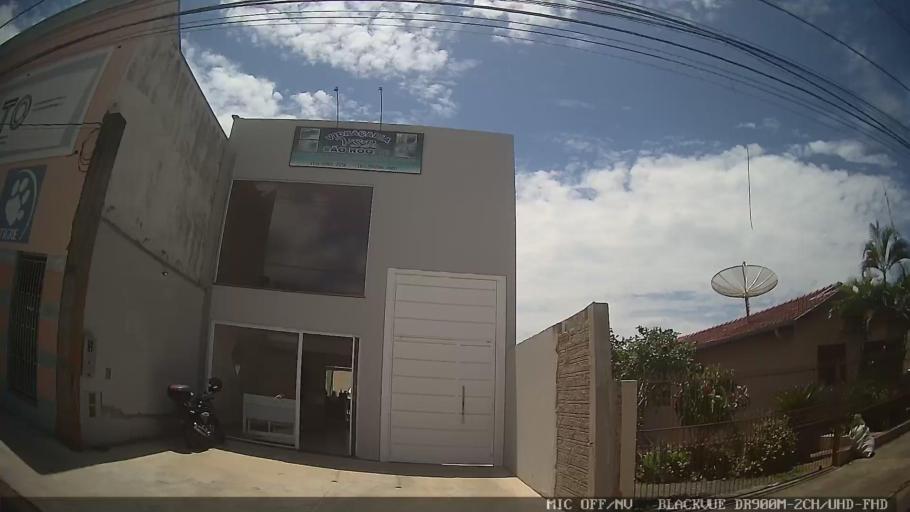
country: BR
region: Sao Paulo
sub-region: Laranjal Paulista
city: Laranjal Paulista
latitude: -23.0412
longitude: -47.8339
